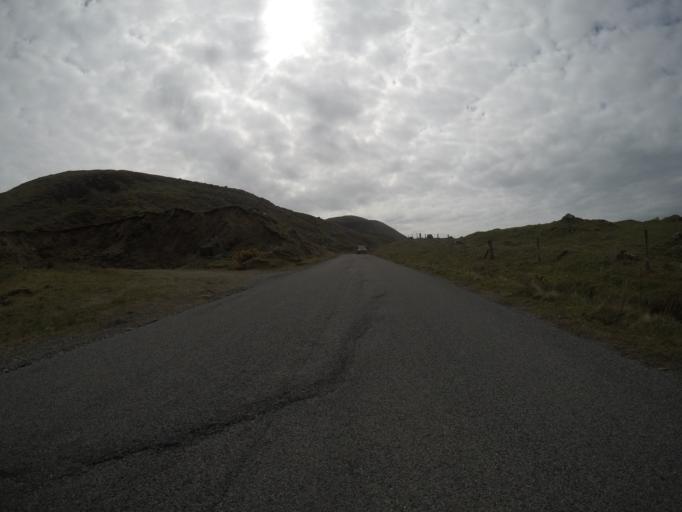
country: GB
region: Scotland
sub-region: Highland
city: Portree
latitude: 57.6700
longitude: -6.3535
